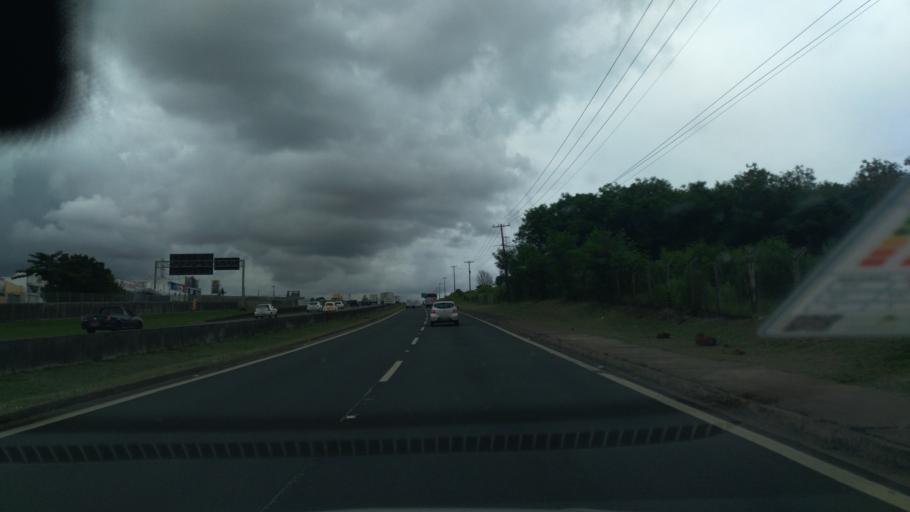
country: BR
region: Sao Paulo
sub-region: Campinas
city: Campinas
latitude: -22.8790
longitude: -47.1186
